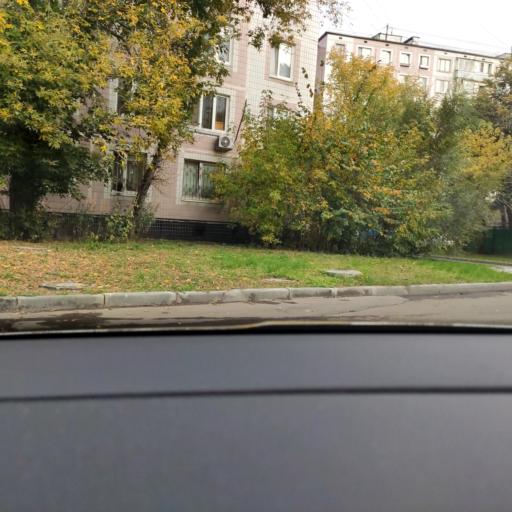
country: RU
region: Moscow
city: Strogino
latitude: 55.8130
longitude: 37.4020
